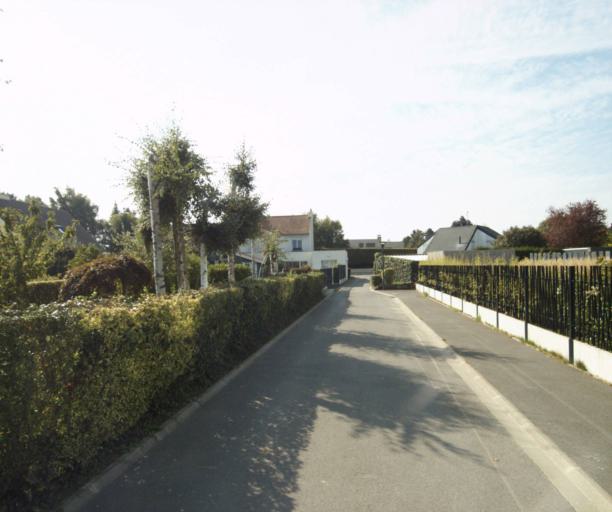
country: FR
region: Nord-Pas-de-Calais
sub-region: Departement du Nord
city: Wattignies
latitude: 50.5755
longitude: 3.0244
